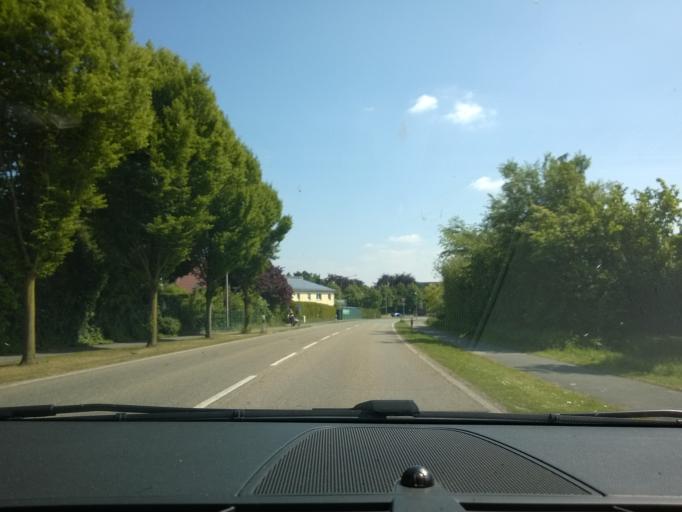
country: DE
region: North Rhine-Westphalia
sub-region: Regierungsbezirk Munster
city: Sudlohn
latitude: 51.9479
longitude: 6.8631
